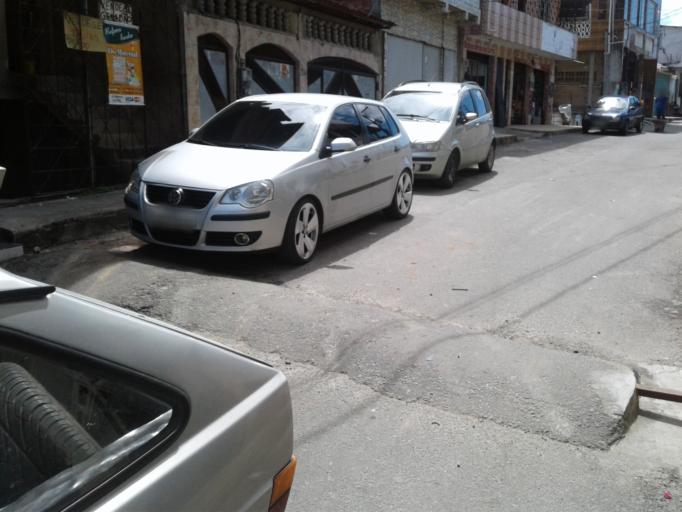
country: BR
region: Bahia
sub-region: Salvador
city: Salvador
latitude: -12.8817
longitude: -38.4733
